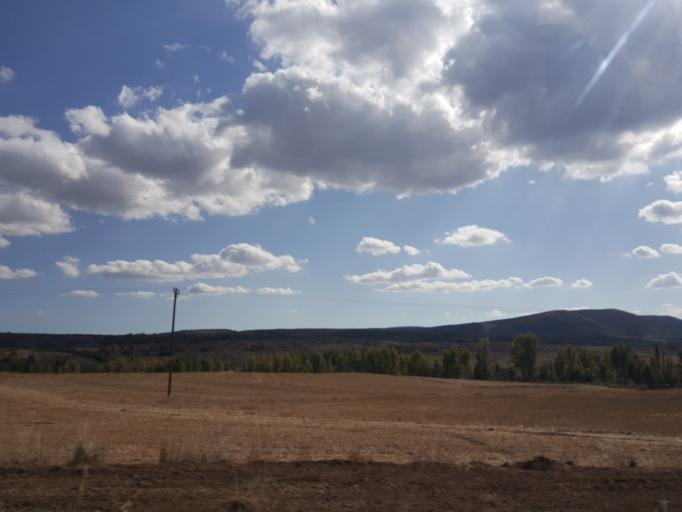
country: TR
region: Tokat
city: Sulusaray
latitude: 39.9750
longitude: 36.0293
